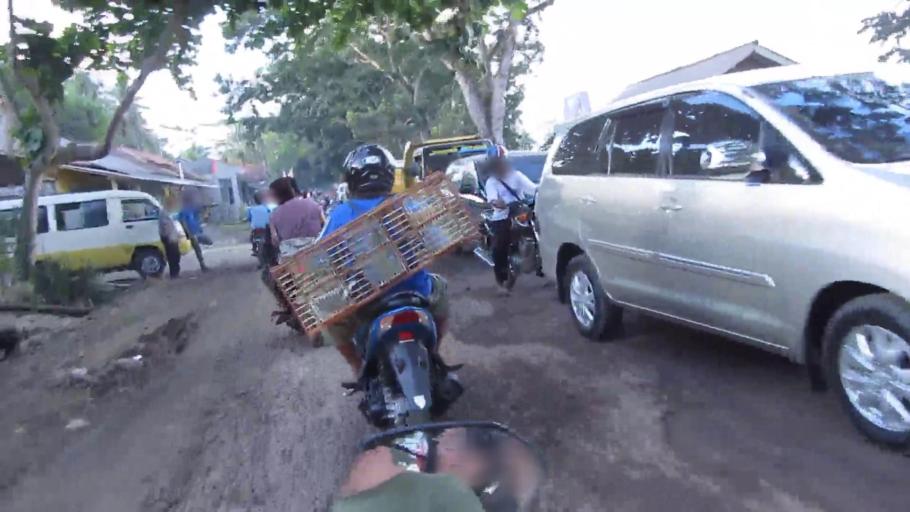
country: ID
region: West Java
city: Balengbeng
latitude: -7.7130
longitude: 108.4881
